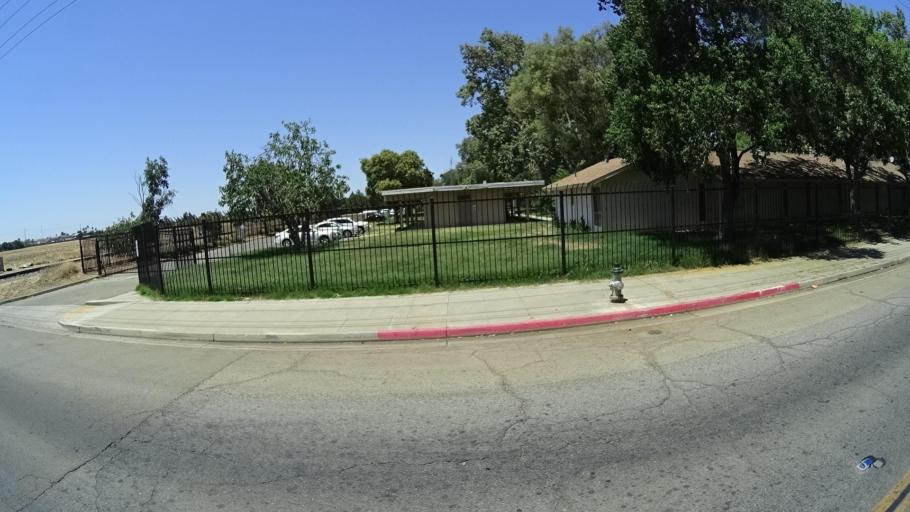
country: US
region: California
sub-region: Fresno County
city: Sunnyside
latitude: 36.7220
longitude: -119.7274
